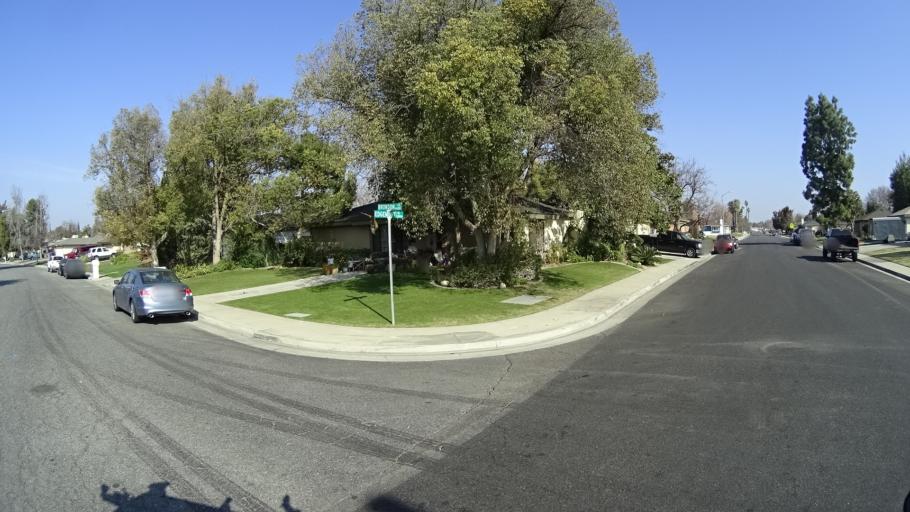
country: US
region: California
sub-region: Kern County
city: Greenacres
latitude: 35.3275
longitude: -119.0720
